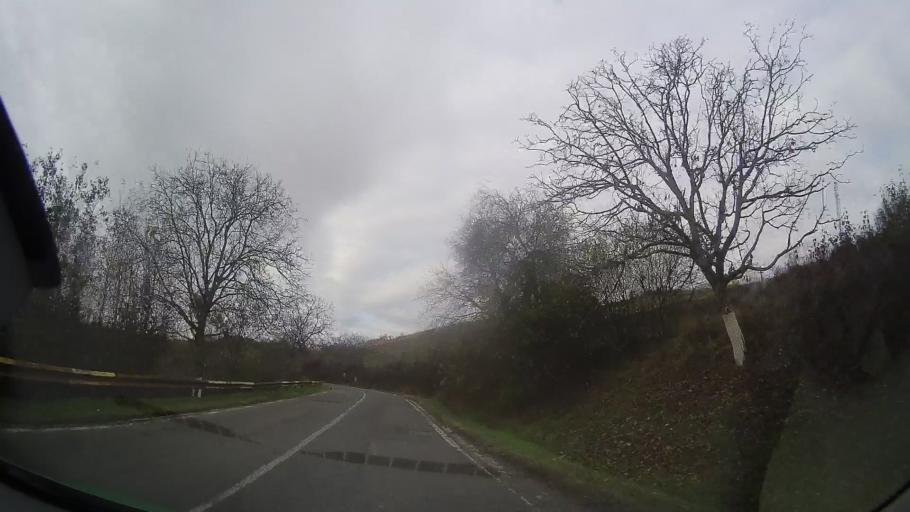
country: RO
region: Bistrita-Nasaud
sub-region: Comuna Silvasu de Campie
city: Silvasu de Campie
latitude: 46.7771
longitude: 24.3222
